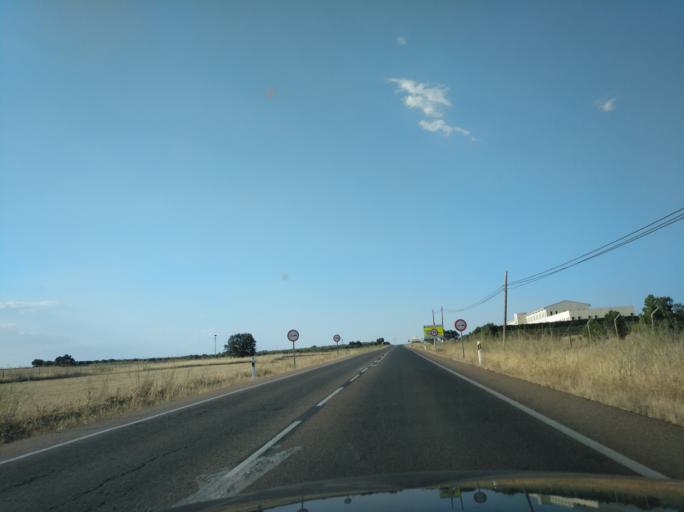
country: ES
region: Extremadura
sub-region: Provincia de Badajoz
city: Olivenza
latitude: 38.7070
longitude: -7.0866
